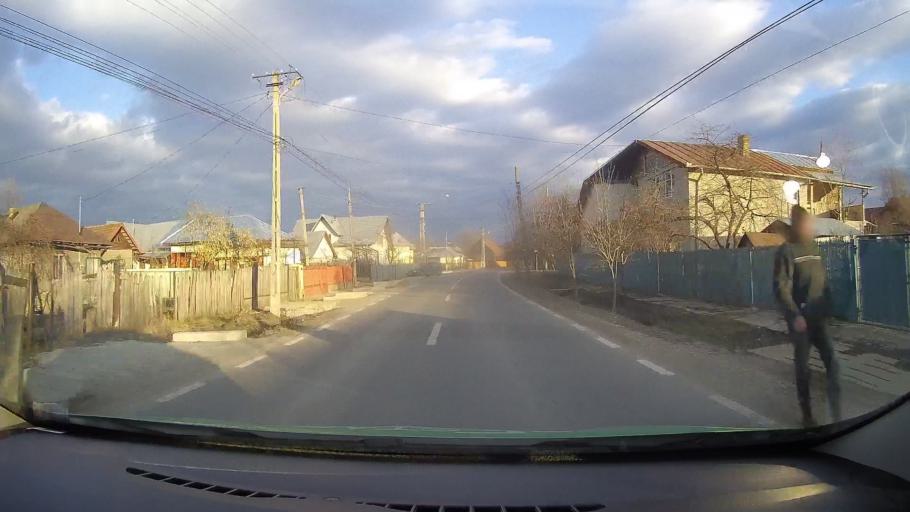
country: RO
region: Dambovita
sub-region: Comuna I. L. Caragiale
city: Ghirdoveni
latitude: 44.9458
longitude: 25.6621
